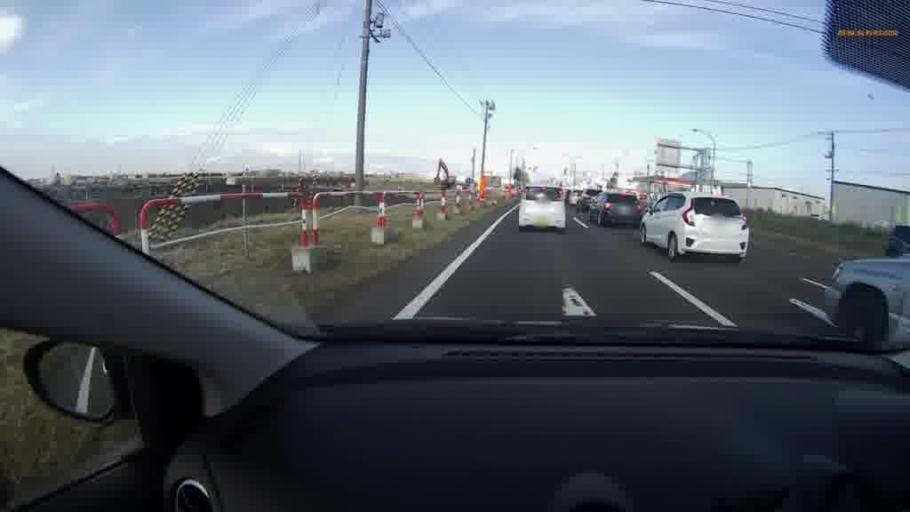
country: JP
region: Hokkaido
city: Kushiro
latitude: 43.0045
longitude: 144.4173
